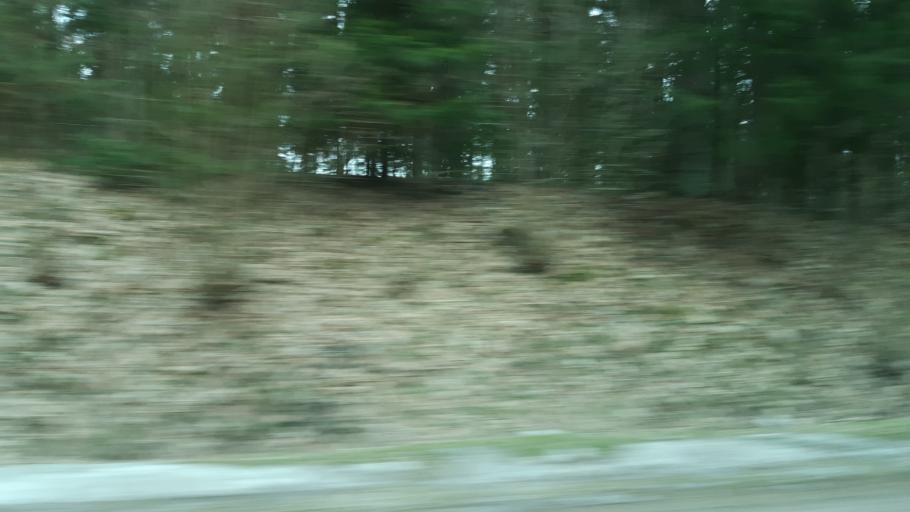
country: PL
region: Podlasie
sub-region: Suwalki
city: Suwalki
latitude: 54.2939
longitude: 22.9583
